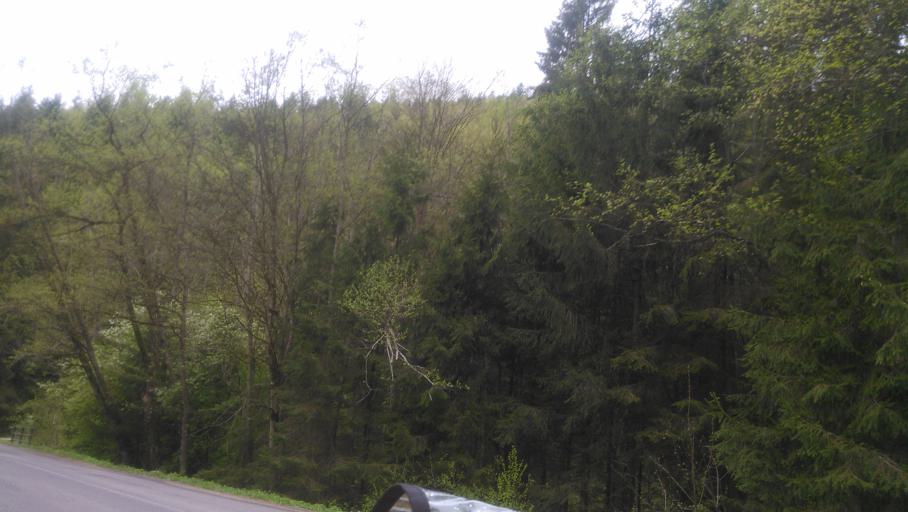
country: SK
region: Banskobystricky
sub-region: Okres Banska Bystrica
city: Brezno
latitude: 48.8600
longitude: 19.6029
